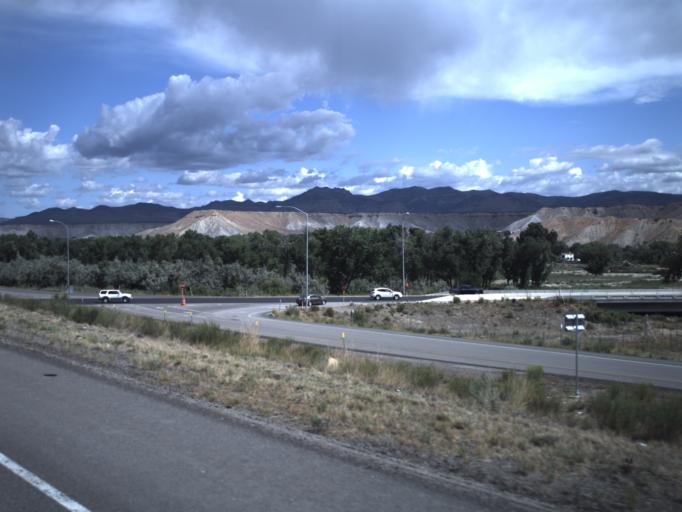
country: US
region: Utah
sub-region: Carbon County
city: Price
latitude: 39.5997
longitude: -110.8263
